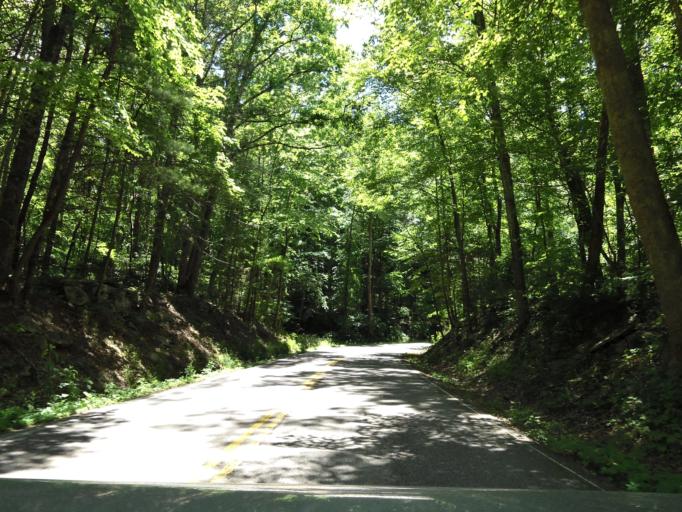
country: US
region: North Carolina
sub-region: Graham County
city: Robbinsville
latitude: 35.4967
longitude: -83.9268
